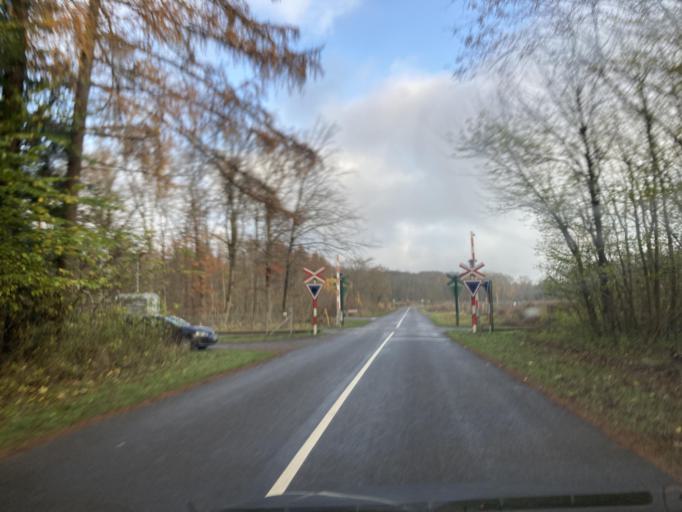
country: DK
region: Zealand
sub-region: Lolland Kommune
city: Rodby
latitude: 54.7842
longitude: 11.3739
